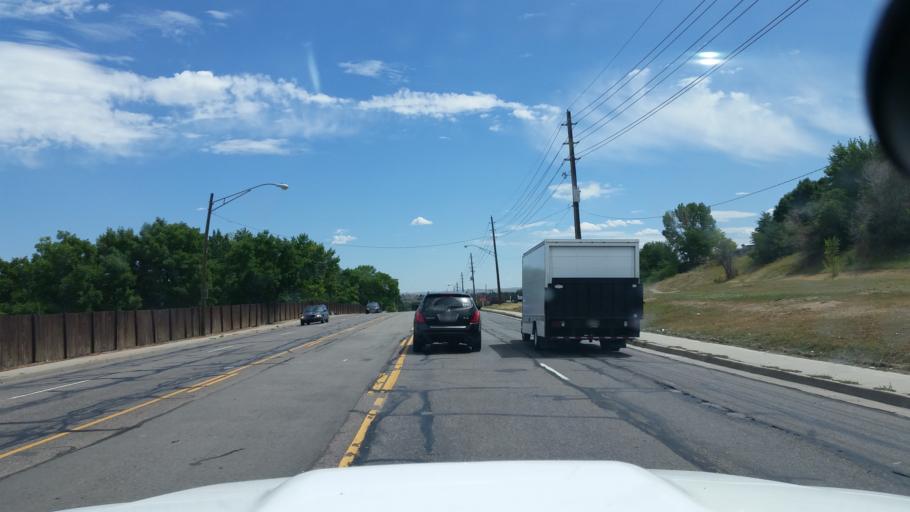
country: US
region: Colorado
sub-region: Adams County
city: Federal Heights
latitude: 39.8635
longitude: -105.0147
